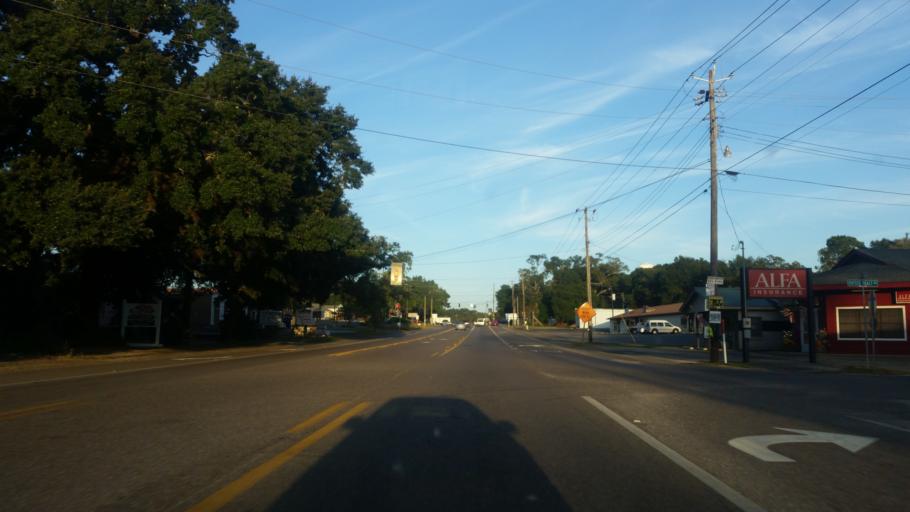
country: US
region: Alabama
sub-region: Mobile County
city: Grand Bay
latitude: 30.4777
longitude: -88.3417
